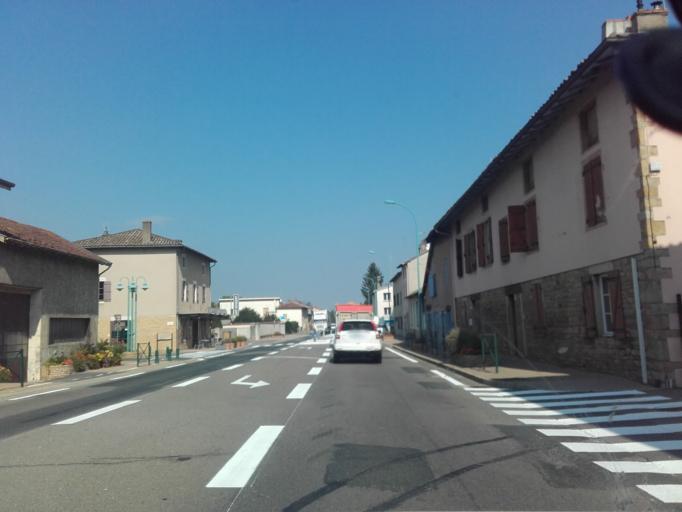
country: FR
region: Bourgogne
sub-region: Departement de Saone-et-Loire
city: Creches-sur-Saone
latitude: 46.2724
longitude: 4.7986
